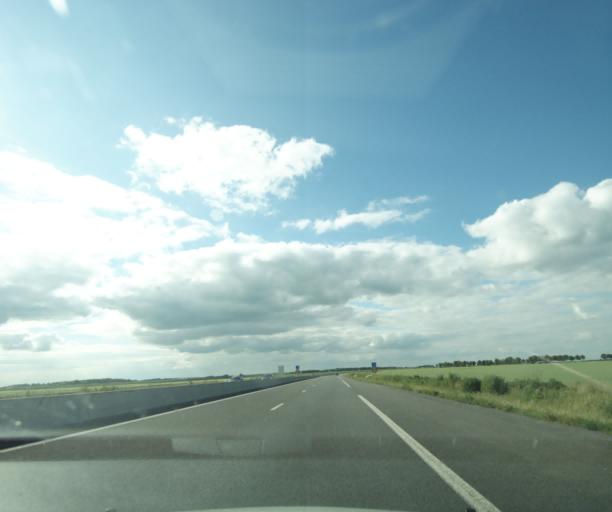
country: FR
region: Centre
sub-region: Departement d'Eure-et-Loir
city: Sours
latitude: 48.3708
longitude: 1.5912
